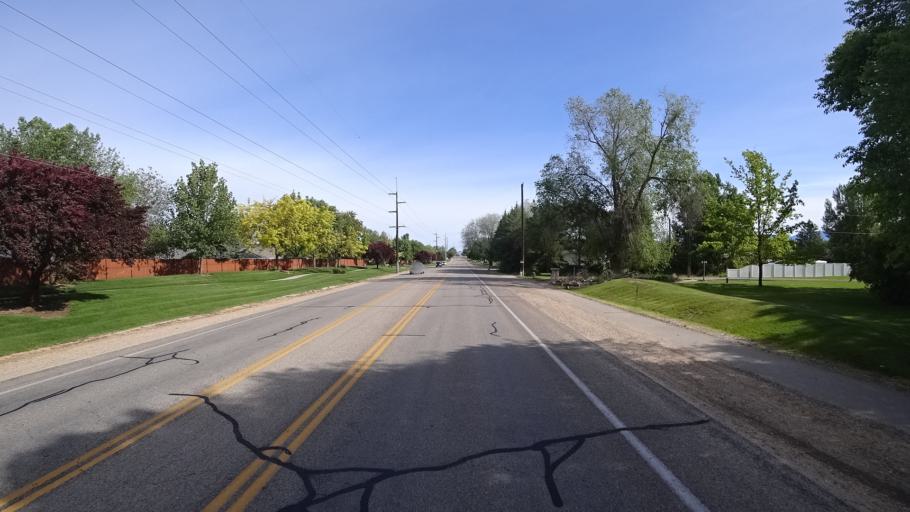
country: US
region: Idaho
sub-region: Ada County
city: Meridian
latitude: 43.5567
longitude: -116.3343
